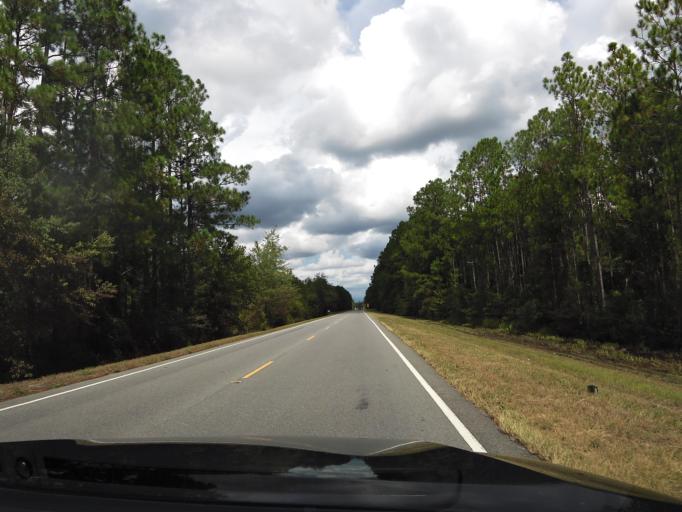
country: US
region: Georgia
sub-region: Brantley County
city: Nahunta
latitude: 31.1352
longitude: -81.9963
